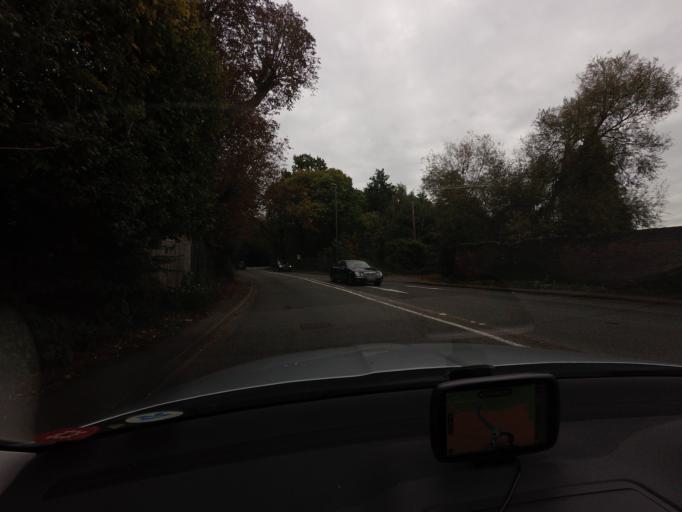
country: GB
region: England
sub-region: Surrey
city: Byfleet
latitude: 51.3412
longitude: -0.4620
